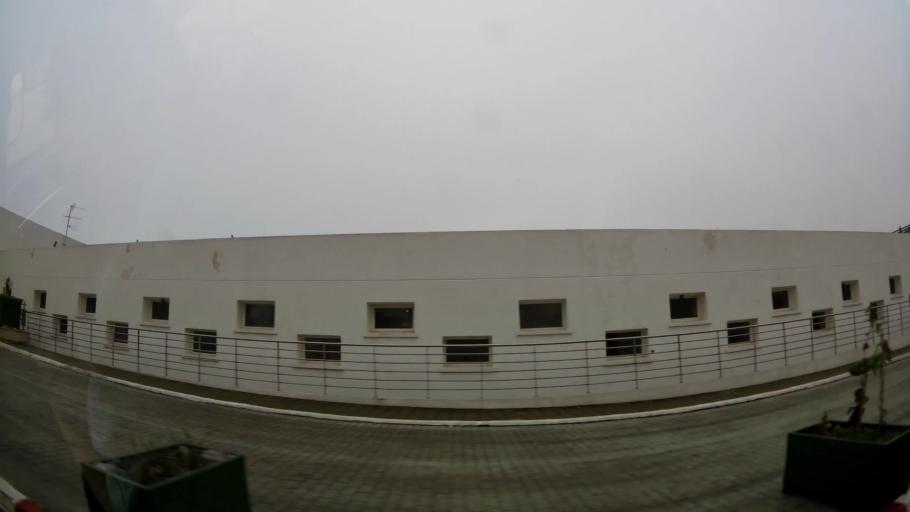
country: MA
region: Taza-Al Hoceima-Taounate
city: Al Hoceima
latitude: 35.2458
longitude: -3.9286
